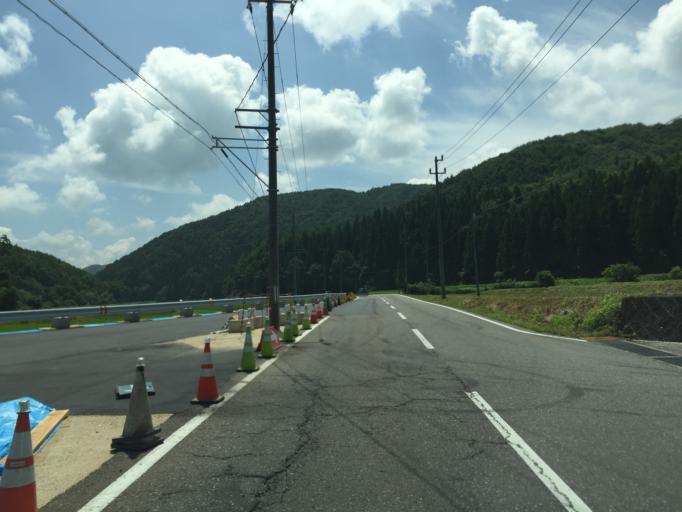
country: JP
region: Fukushima
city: Inawashiro
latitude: 37.4274
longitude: 140.0275
